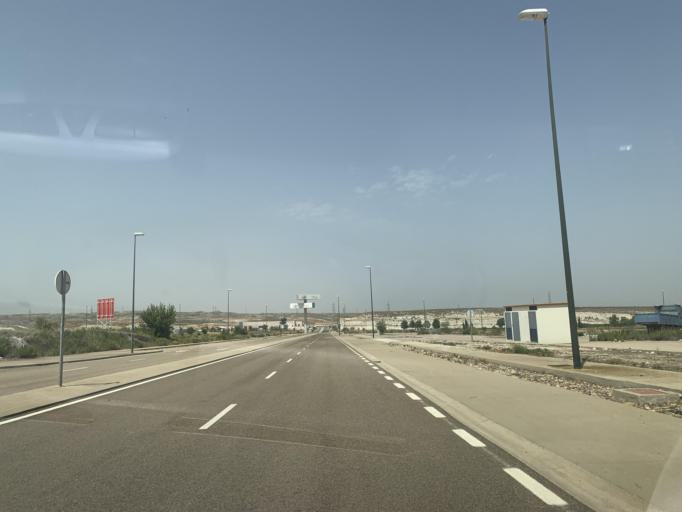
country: ES
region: Aragon
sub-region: Provincia de Zaragoza
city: Zaragoza
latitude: 41.5854
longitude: -0.8343
